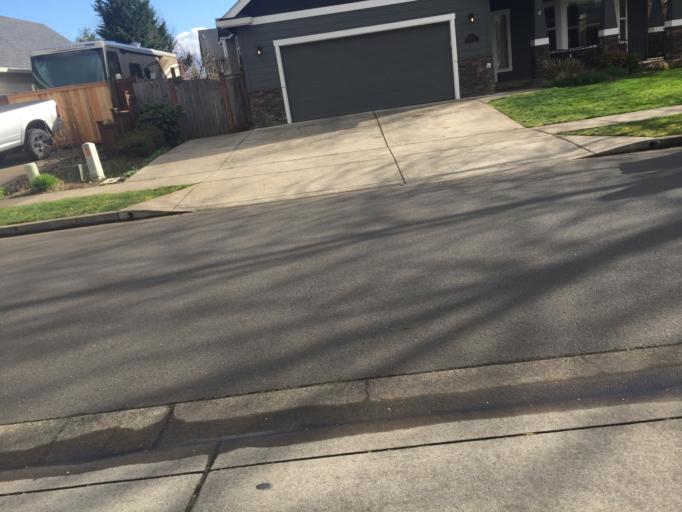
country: US
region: Oregon
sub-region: Lane County
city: Eugene
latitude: 44.1015
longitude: -123.1563
